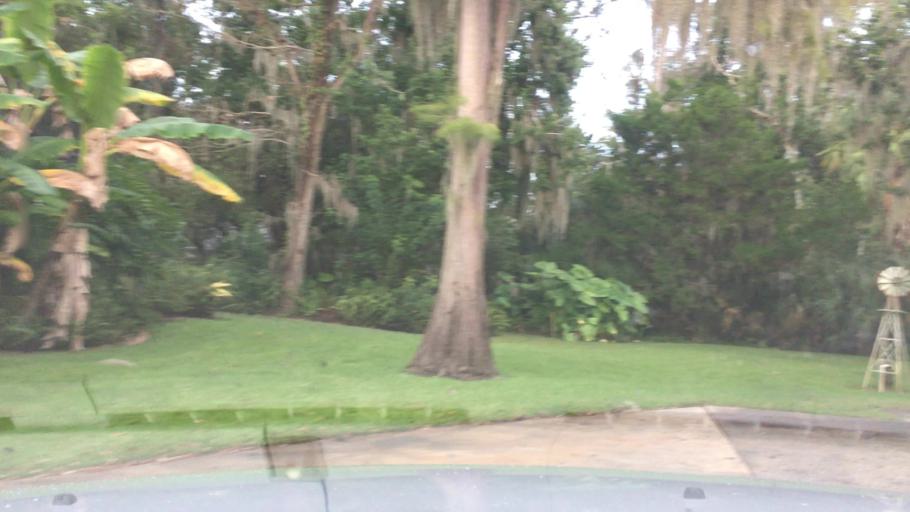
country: US
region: Florida
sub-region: Volusia County
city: Ormond-by-the-Sea
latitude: 29.3341
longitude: -81.1160
